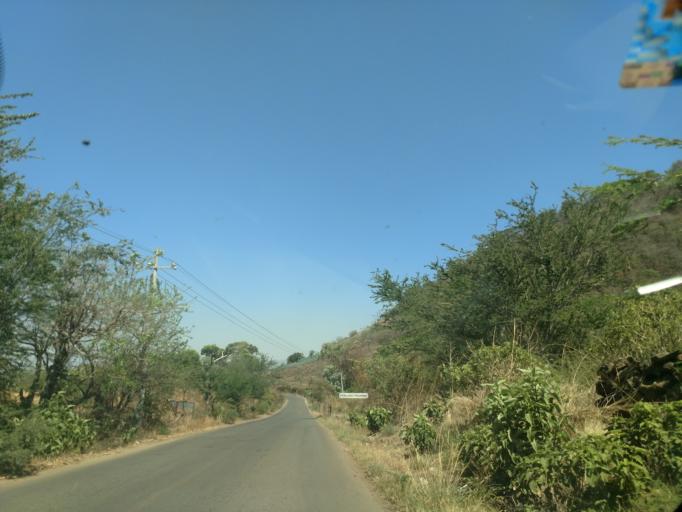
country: MX
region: Nayarit
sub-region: Tepic
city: La Corregidora
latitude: 21.4733
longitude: -104.6689
